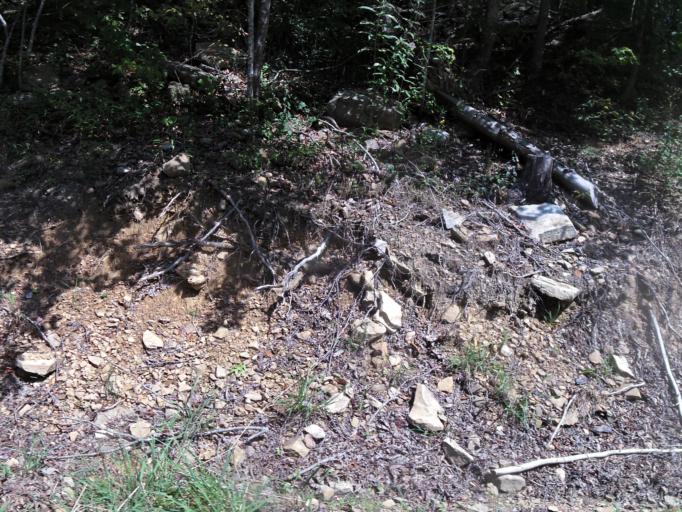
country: US
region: Kentucky
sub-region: Harlan County
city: Harlan
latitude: 36.8762
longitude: -83.3191
